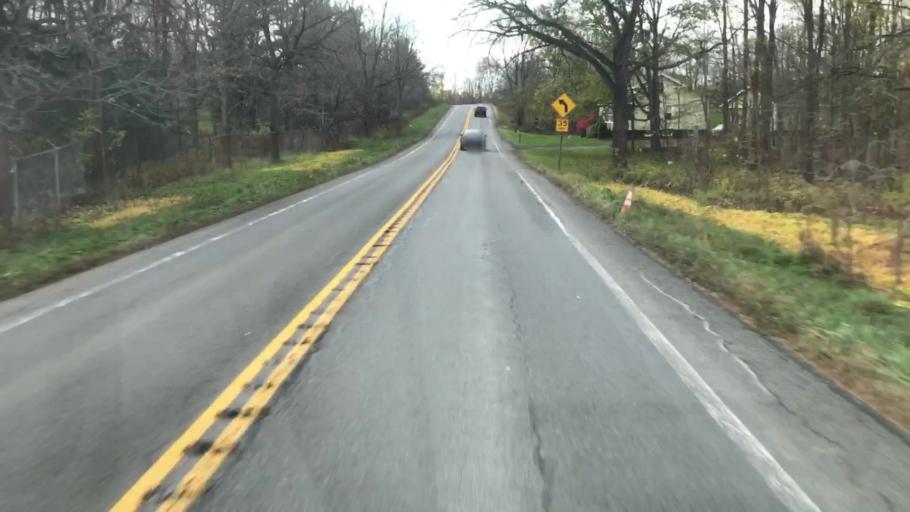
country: US
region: New York
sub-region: Onondaga County
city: Elbridge
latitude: 43.0024
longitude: -76.4235
